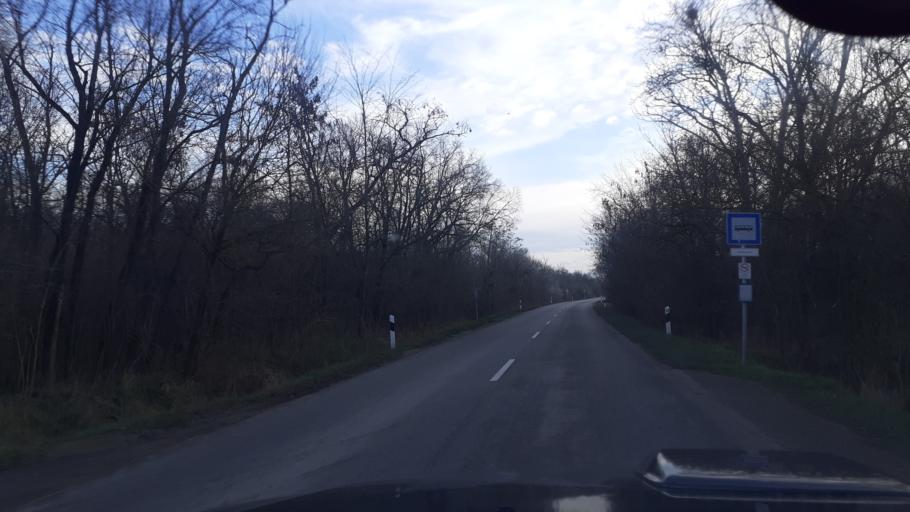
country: HU
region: Bacs-Kiskun
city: Szabadszallas
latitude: 46.9325
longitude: 19.1717
